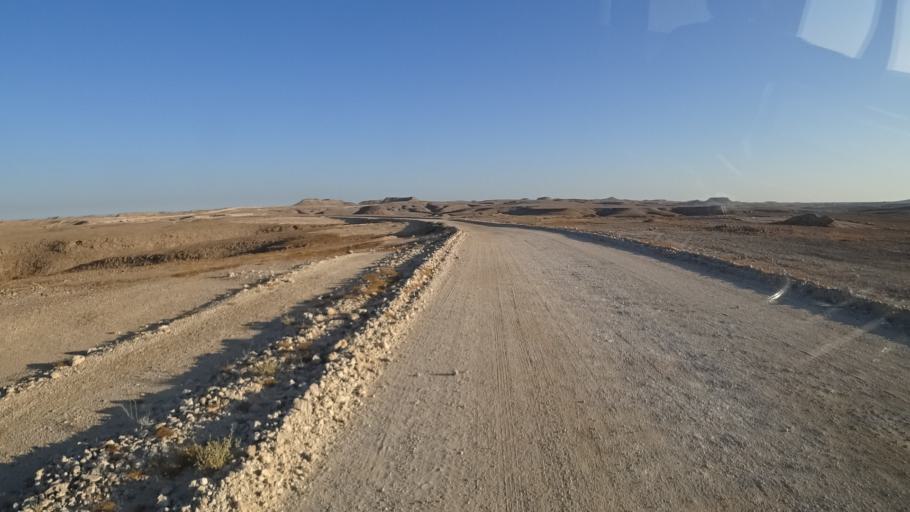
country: YE
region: Al Mahrah
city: Hawf
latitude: 17.1559
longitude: 53.3501
